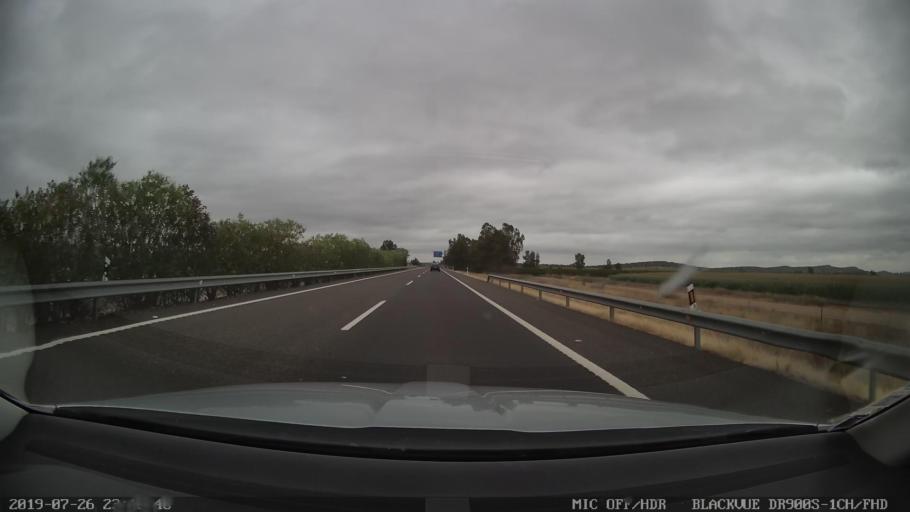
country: ES
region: Extremadura
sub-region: Provincia de Badajoz
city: Santa Amalia
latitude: 39.0267
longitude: -6.0761
